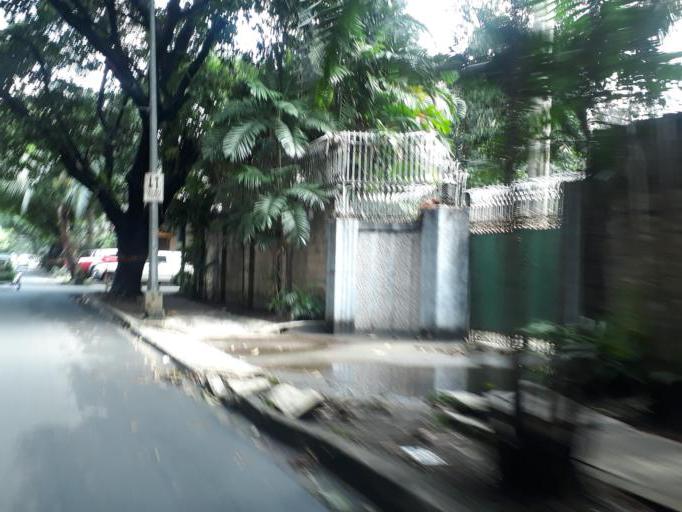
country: PH
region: Metro Manila
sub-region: San Juan
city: San Juan
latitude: 14.6185
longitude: 121.0291
